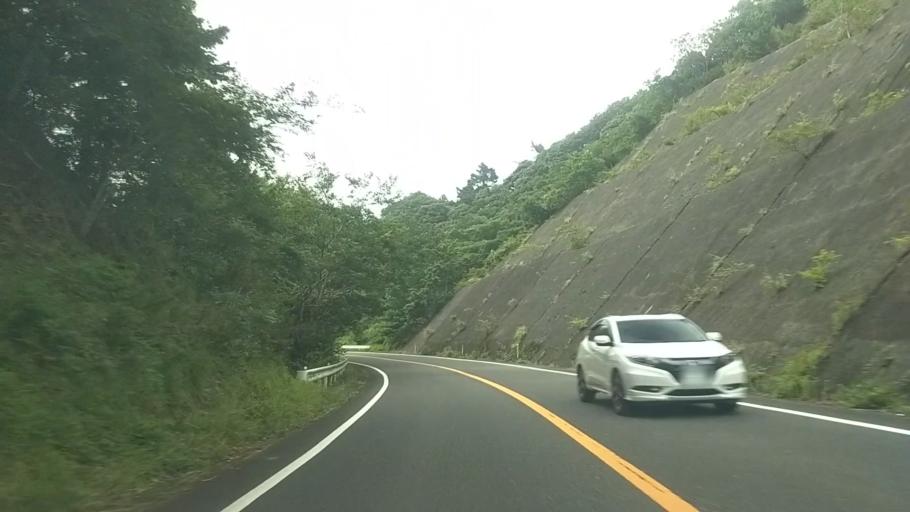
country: JP
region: Chiba
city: Kawaguchi
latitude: 35.2130
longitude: 140.0519
